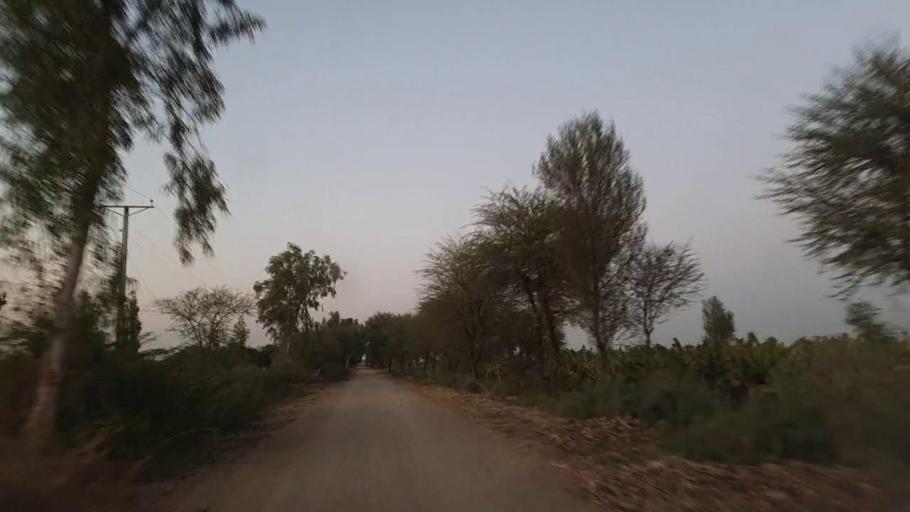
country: PK
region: Sindh
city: Samaro
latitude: 25.3418
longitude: 69.3978
